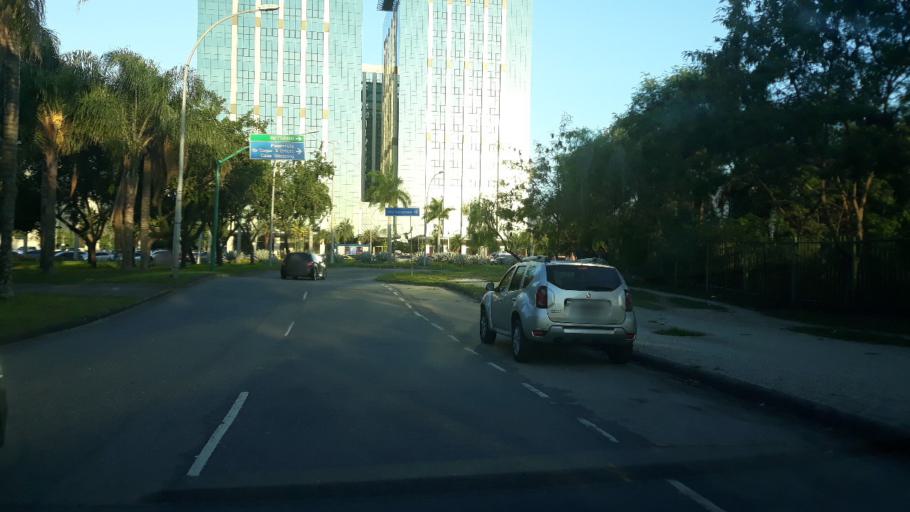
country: BR
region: Rio de Janeiro
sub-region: Rio De Janeiro
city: Rio de Janeiro
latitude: -22.9848
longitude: -43.3609
